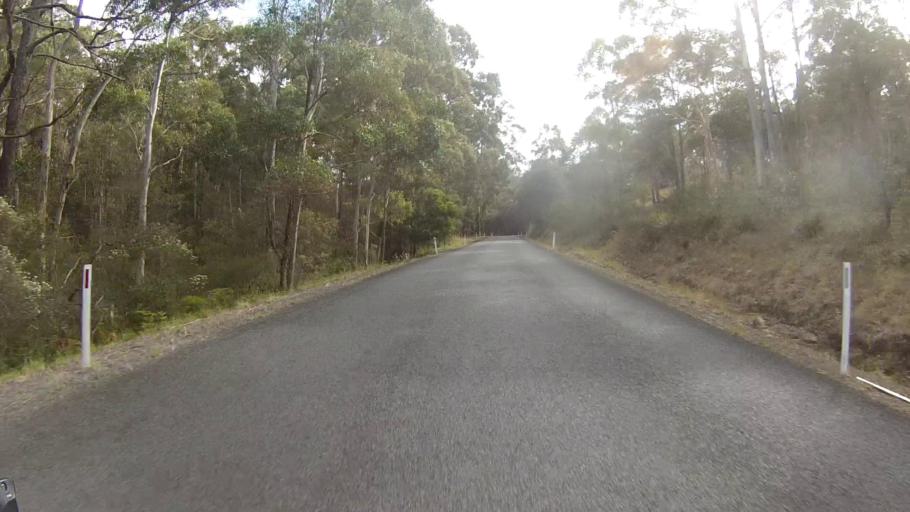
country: AU
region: Tasmania
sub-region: Sorell
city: Sorell
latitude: -42.8125
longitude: 147.7924
